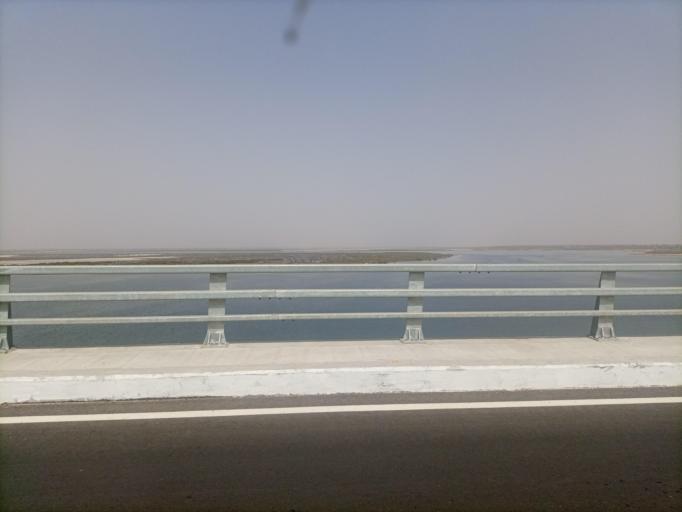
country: SN
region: Fatick
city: Foundiougne
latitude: 14.1360
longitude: -16.4687
